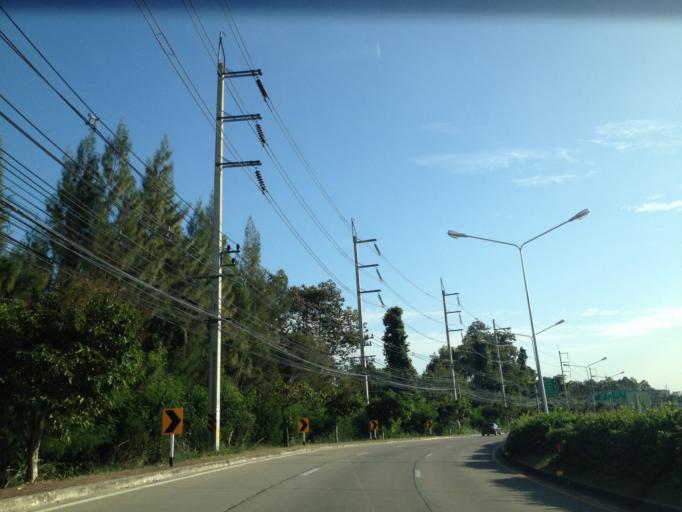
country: TH
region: Chiang Mai
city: Chiang Mai
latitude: 18.8264
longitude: 98.9657
